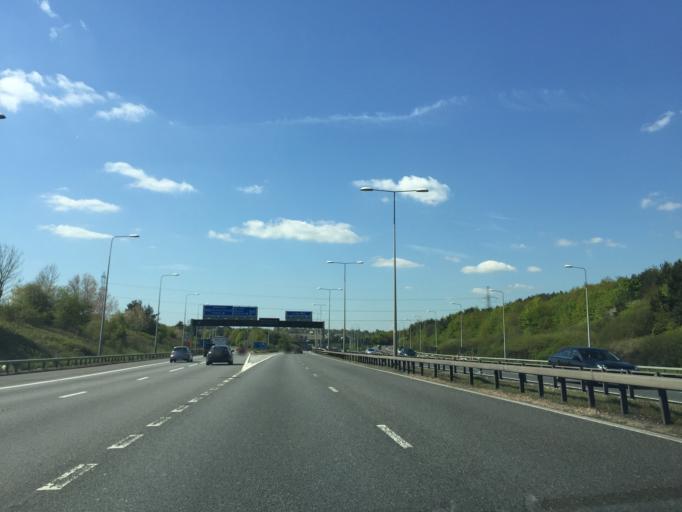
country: GB
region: England
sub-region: Essex
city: Epping
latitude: 51.6846
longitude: 0.1316
